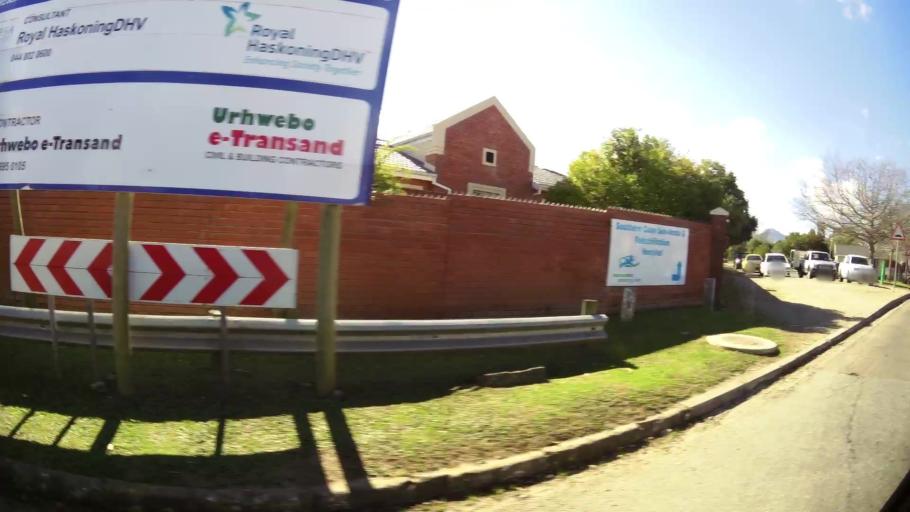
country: ZA
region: Western Cape
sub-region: Eden District Municipality
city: George
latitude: -33.9443
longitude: 22.4744
